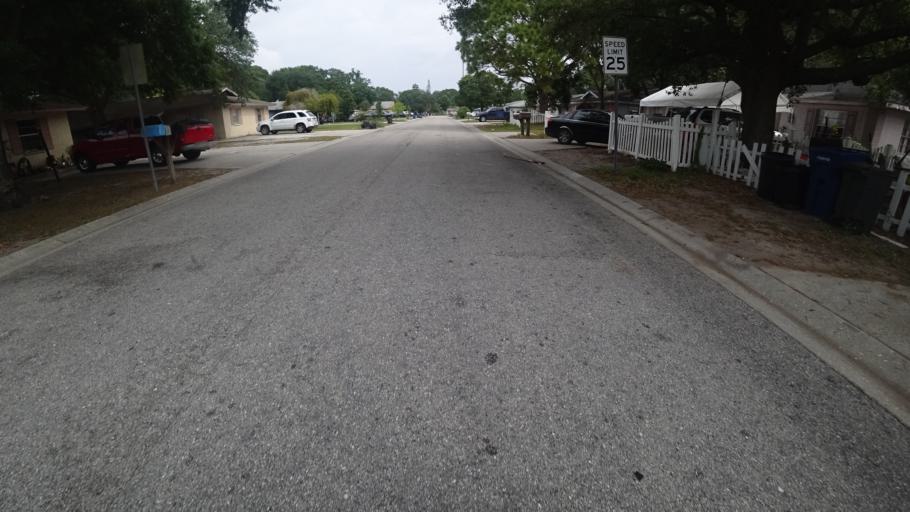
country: US
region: Florida
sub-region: Manatee County
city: West Samoset
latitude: 27.4634
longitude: -82.5558
